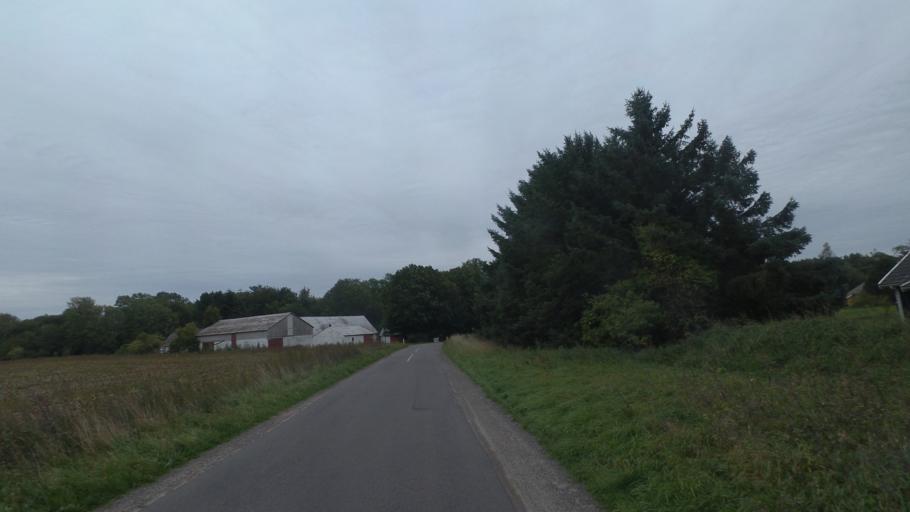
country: DK
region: Capital Region
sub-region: Bornholm Kommune
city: Akirkeby
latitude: 55.0060
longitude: 14.9921
